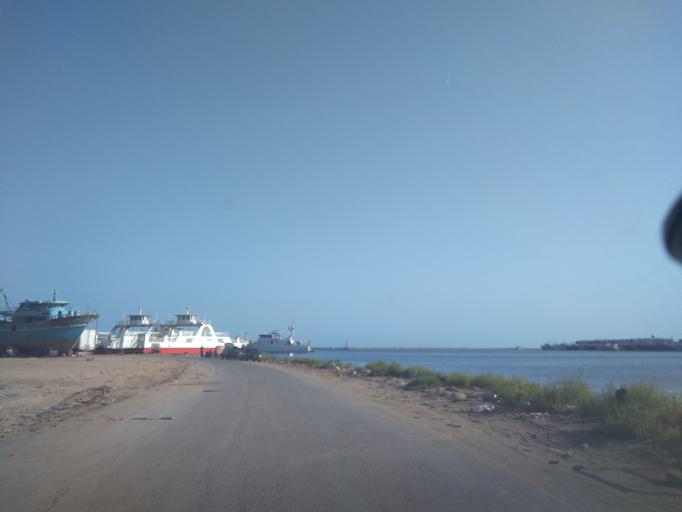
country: TN
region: Safaqis
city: Sfax
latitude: 34.7180
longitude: 10.7675
